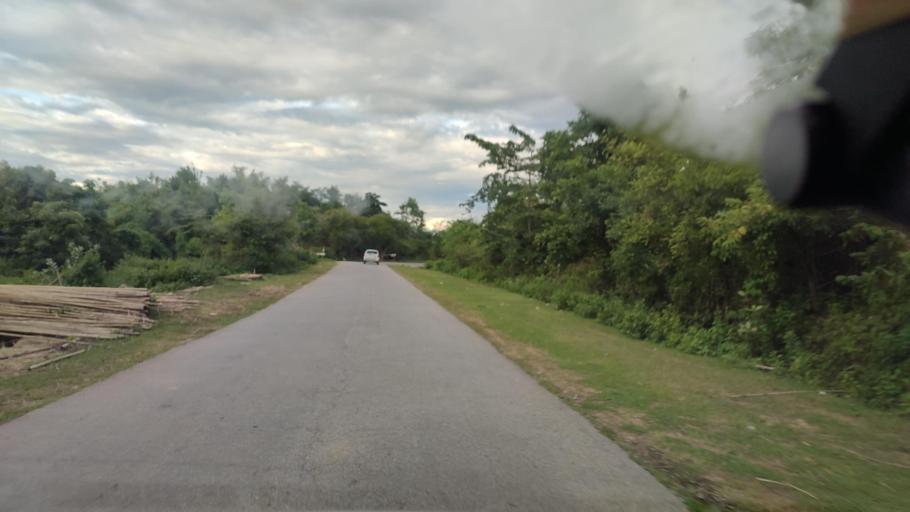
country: MM
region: Mandalay
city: Nay Pyi Taw
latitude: 19.9973
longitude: 95.9291
